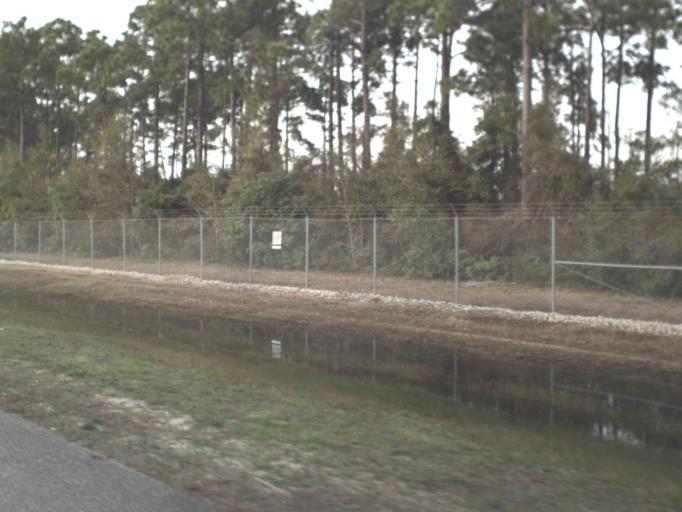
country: US
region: Florida
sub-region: Bay County
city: Tyndall Air Force Base
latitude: 30.0559
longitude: -85.5720
